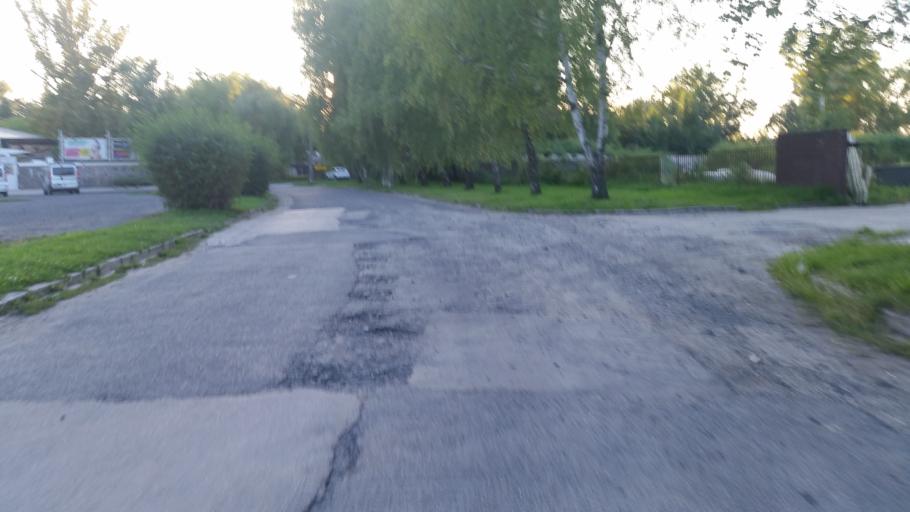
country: HU
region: Somogy
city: Siofok
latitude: 46.9012
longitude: 18.0176
